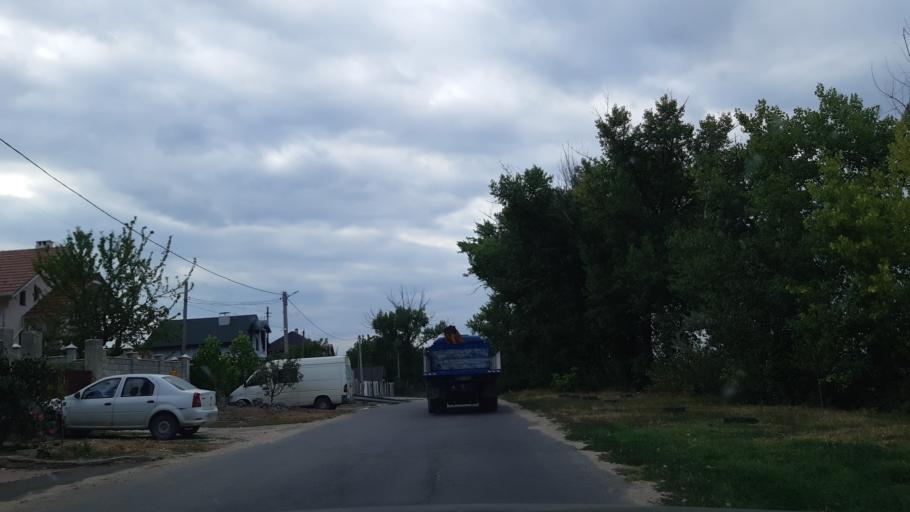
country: MD
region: Chisinau
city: Vatra
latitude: 47.0532
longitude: 28.7324
